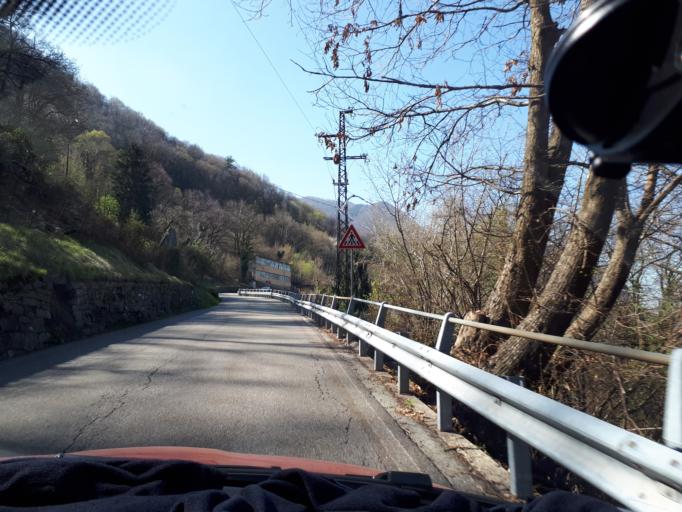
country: IT
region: Lombardy
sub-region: Provincia di Como
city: Faggeto Lario
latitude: 45.8598
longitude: 9.1486
